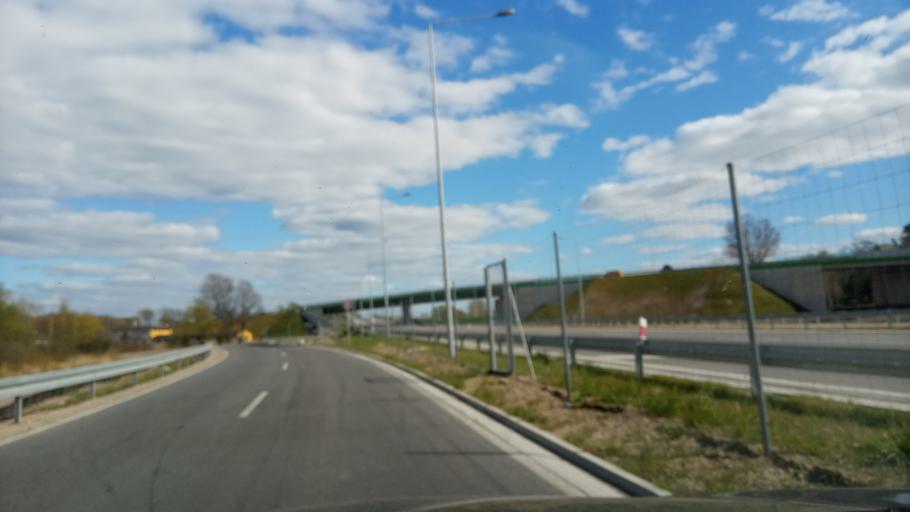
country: PL
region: West Pomeranian Voivodeship
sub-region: Powiat szczecinecki
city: Szczecinek
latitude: 53.7144
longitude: 16.7105
